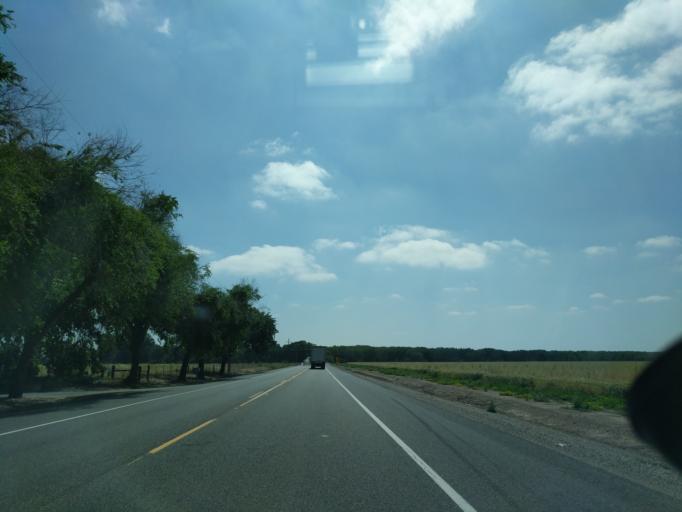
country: US
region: California
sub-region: San Joaquin County
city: Linden
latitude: 37.9355
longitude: -121.0877
